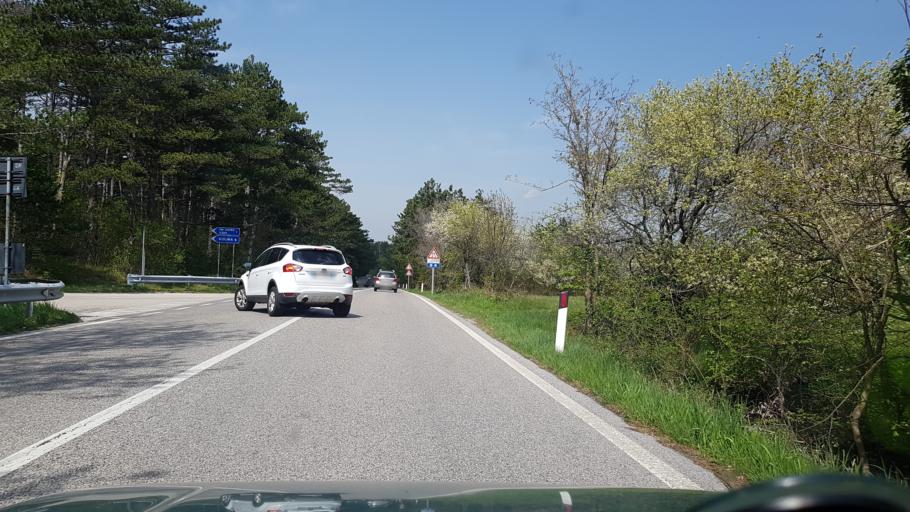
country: IT
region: Friuli Venezia Giulia
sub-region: Provincia di Trieste
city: Dolina
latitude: 45.6326
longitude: 13.8859
